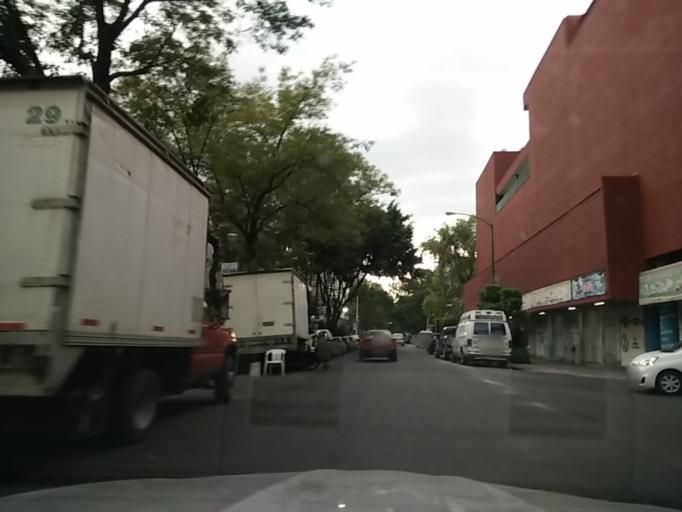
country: MX
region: Mexico City
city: Cuauhtemoc
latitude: 19.4243
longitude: -99.1542
